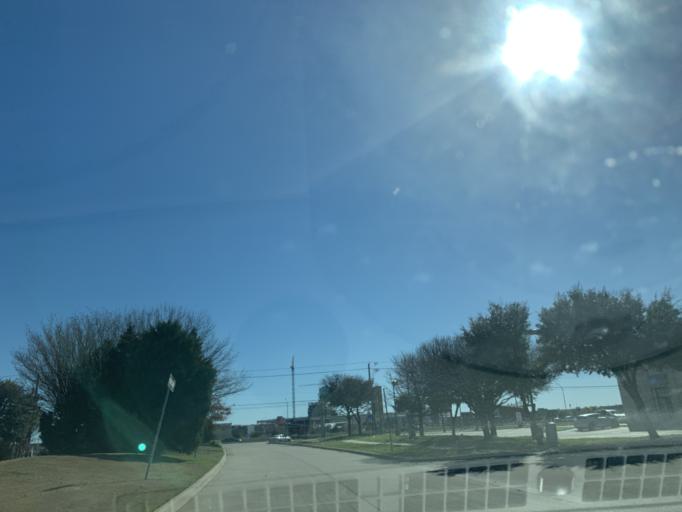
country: US
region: Texas
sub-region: Denton County
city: The Colony
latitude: 33.0794
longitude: -96.8623
